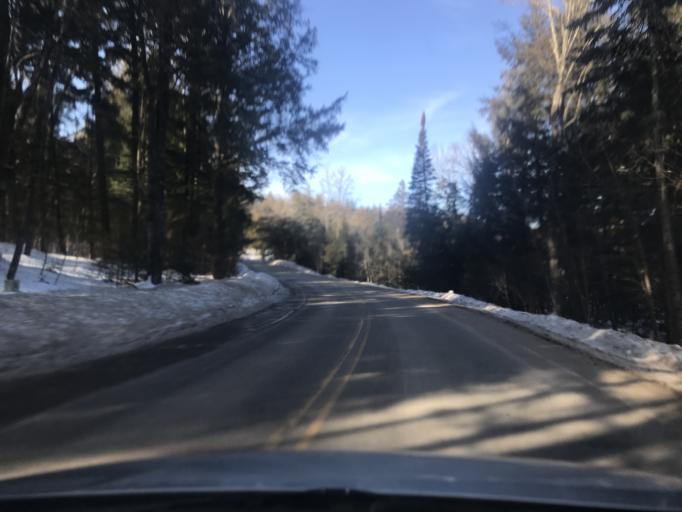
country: US
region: Michigan
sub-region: Dickinson County
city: Kingsford
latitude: 45.4105
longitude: -88.3543
